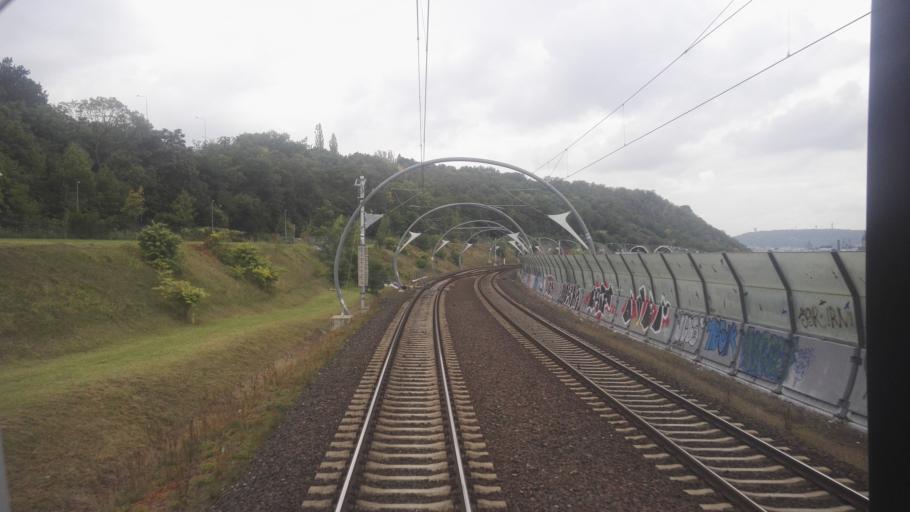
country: CZ
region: Praha
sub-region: Praha 8
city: Liben
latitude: 50.0937
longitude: 14.4702
